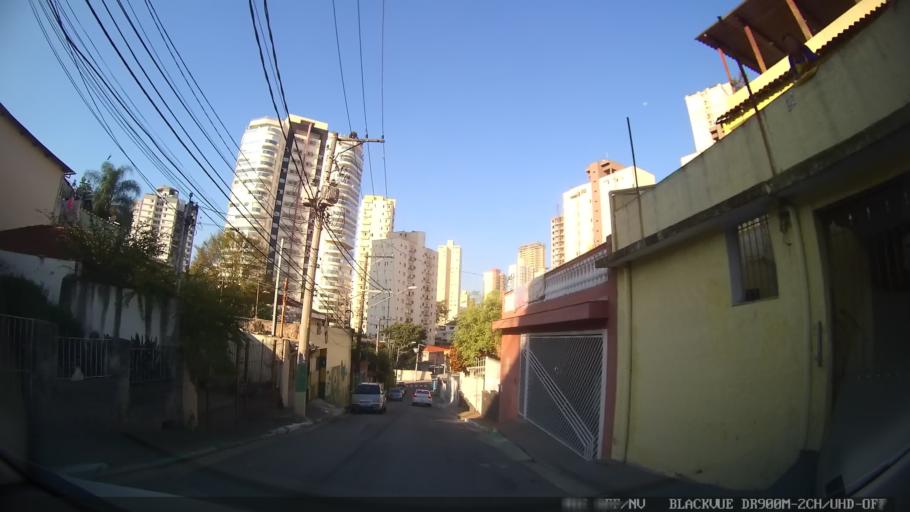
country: BR
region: Sao Paulo
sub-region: Sao Paulo
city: Sao Paulo
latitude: -23.4900
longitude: -46.6410
